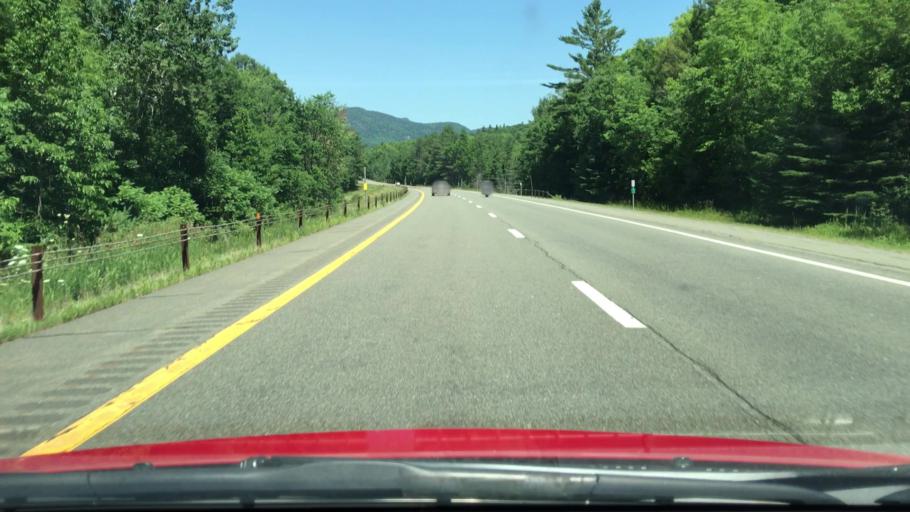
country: US
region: New York
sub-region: Essex County
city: Elizabethtown
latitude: 44.3412
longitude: -73.5326
